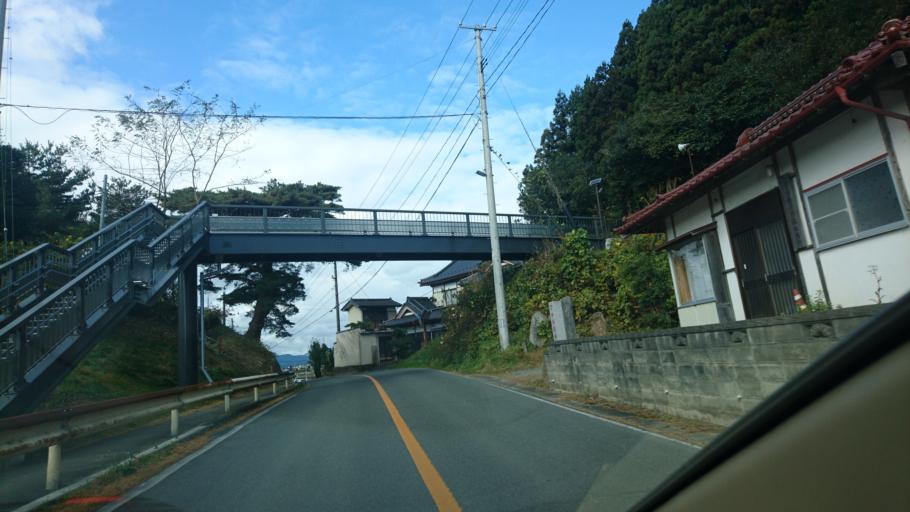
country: JP
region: Iwate
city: Ofunato
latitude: 38.9965
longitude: 141.6968
